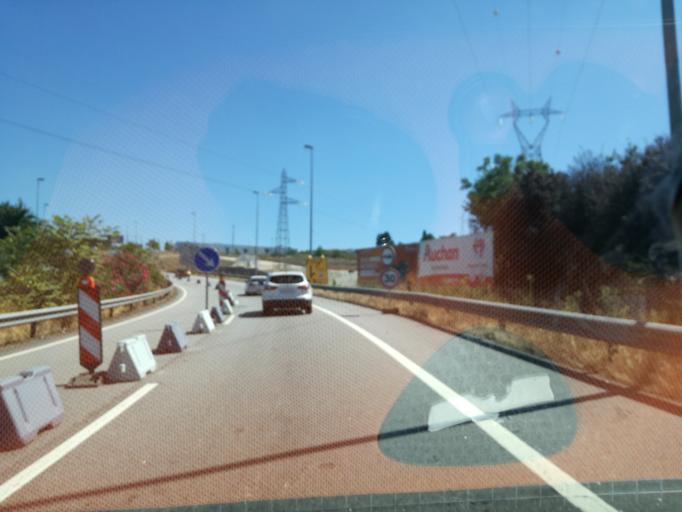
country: PT
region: Braga
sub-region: Guimaraes
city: Candoso
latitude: 41.4421
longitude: -8.3362
